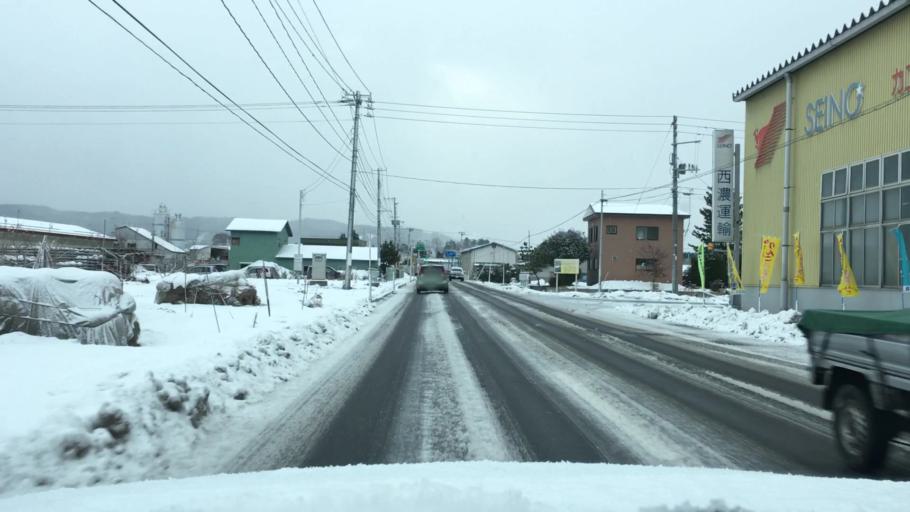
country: JP
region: Aomori
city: Hirosaki
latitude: 40.5576
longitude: 140.5347
